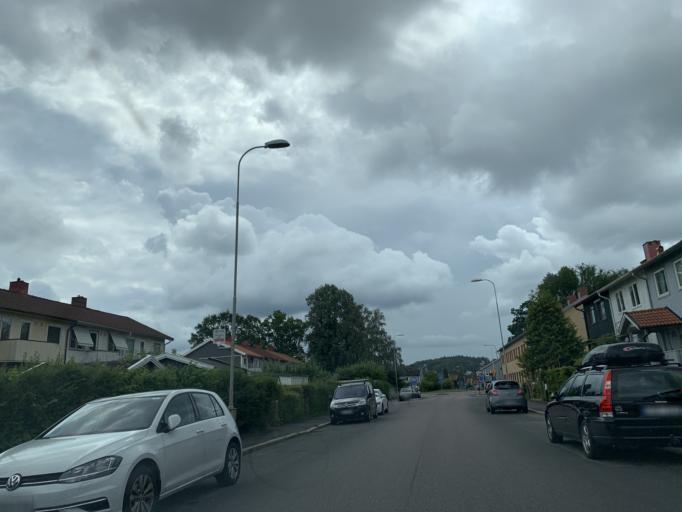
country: SE
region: Vaestra Goetaland
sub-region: Goteborg
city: Eriksbo
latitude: 57.7386
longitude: 12.0591
